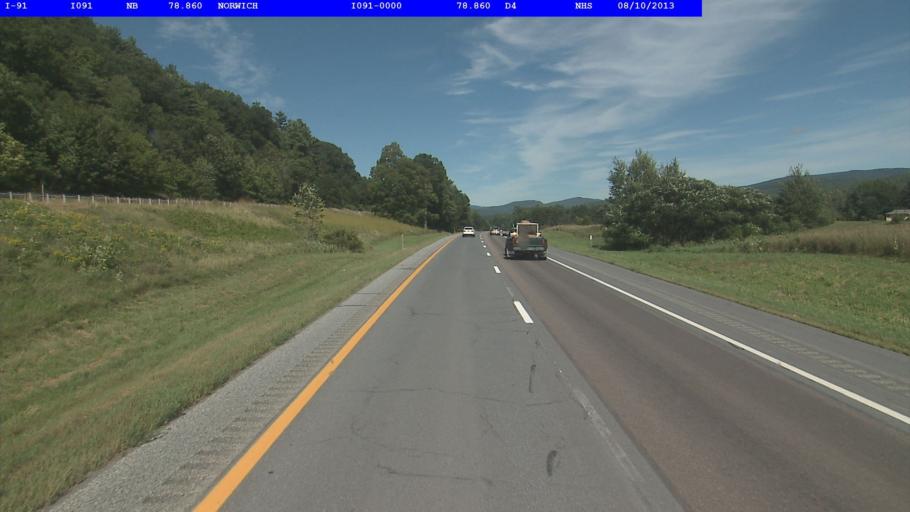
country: US
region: New Hampshire
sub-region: Grafton County
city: Hanover
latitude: 43.7480
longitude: -72.2528
